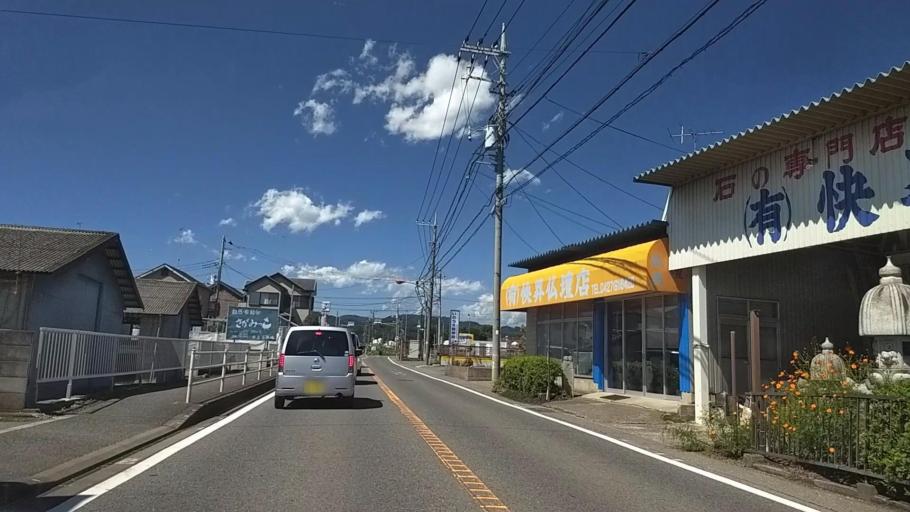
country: JP
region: Tokyo
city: Hachioji
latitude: 35.5819
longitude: 139.3131
